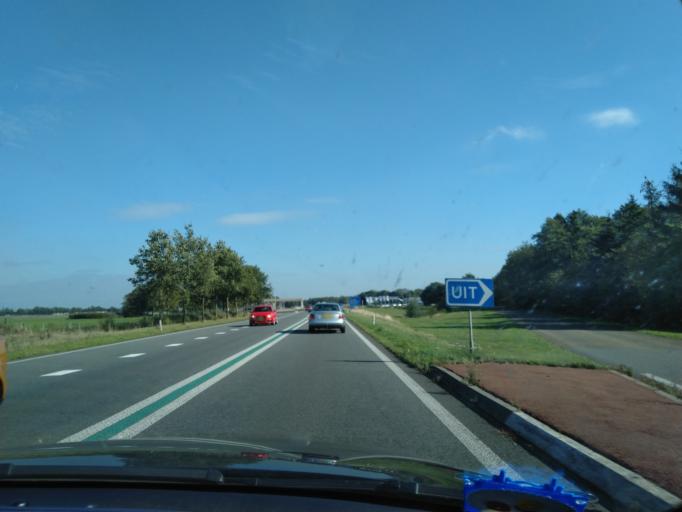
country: NL
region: Groningen
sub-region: Gemeente Pekela
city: Oude Pekela
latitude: 53.0889
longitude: 6.9506
